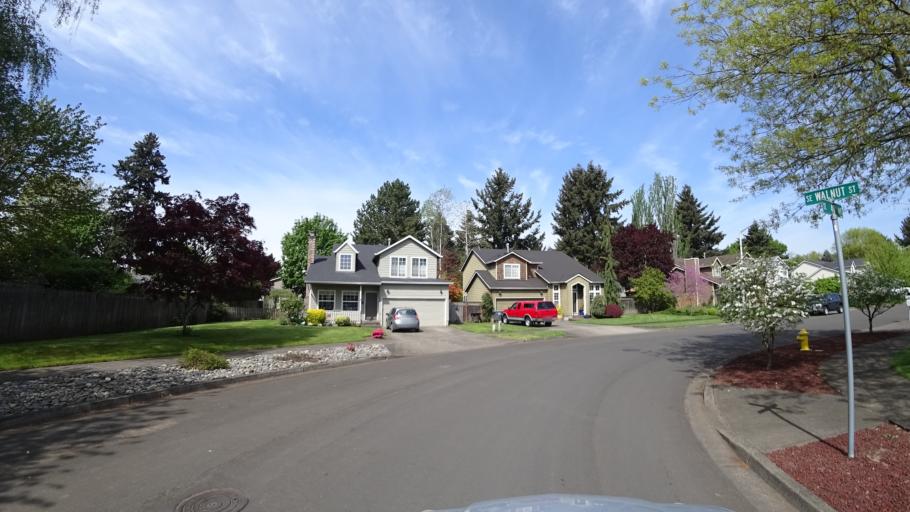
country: US
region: Oregon
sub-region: Washington County
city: Hillsboro
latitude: 45.5168
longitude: -122.9407
